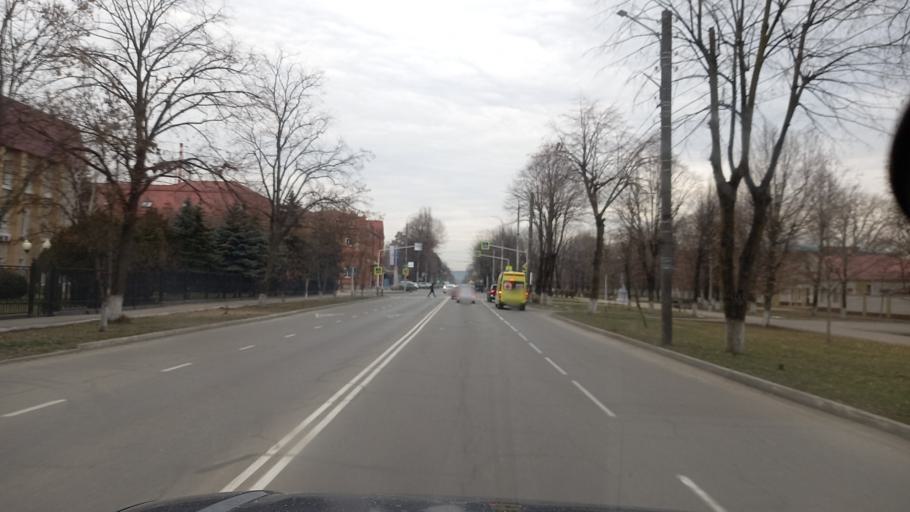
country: RU
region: Adygeya
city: Maykop
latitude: 44.6008
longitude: 40.1066
